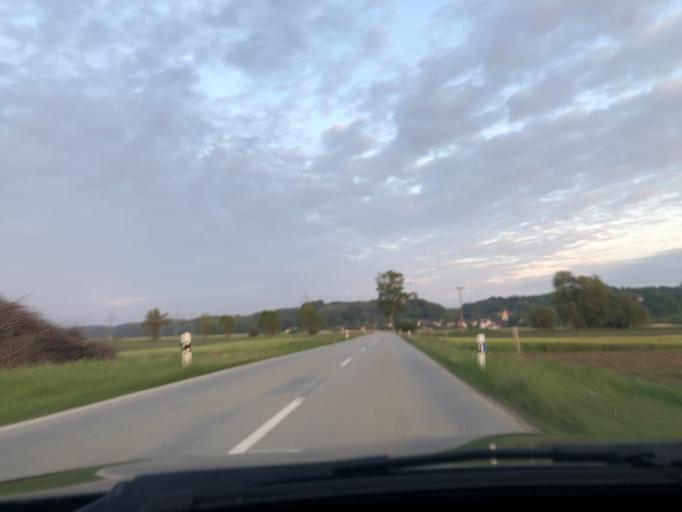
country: DE
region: Bavaria
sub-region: Upper Bavaria
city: Wolfersdorf
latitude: 48.4478
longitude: 11.7154
